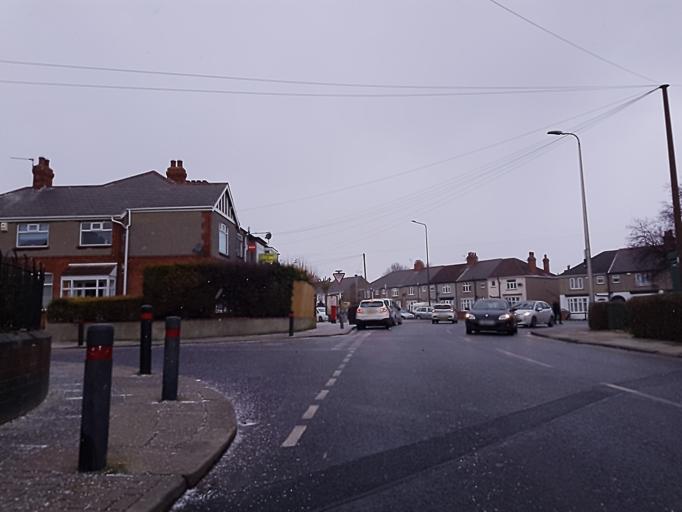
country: GB
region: England
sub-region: North East Lincolnshire
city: Grimbsy
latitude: 53.5625
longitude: -0.1098
